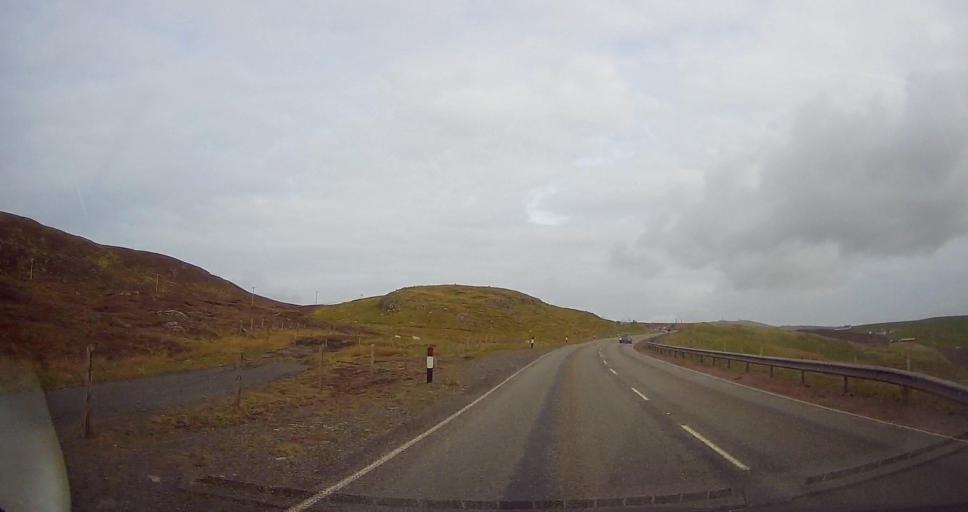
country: GB
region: Scotland
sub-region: Shetland Islands
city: Lerwick
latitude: 60.1077
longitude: -1.2190
